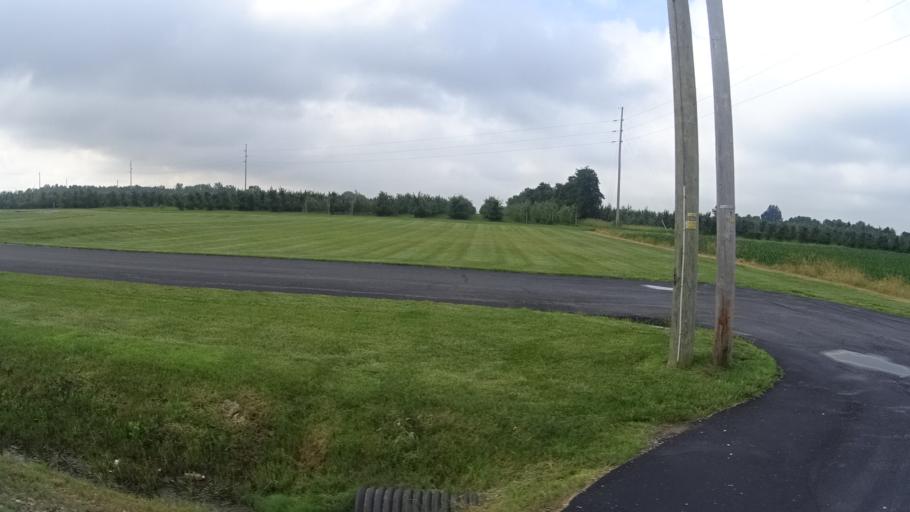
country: US
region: Ohio
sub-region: Huron County
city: Wakeman
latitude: 41.3047
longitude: -82.4946
